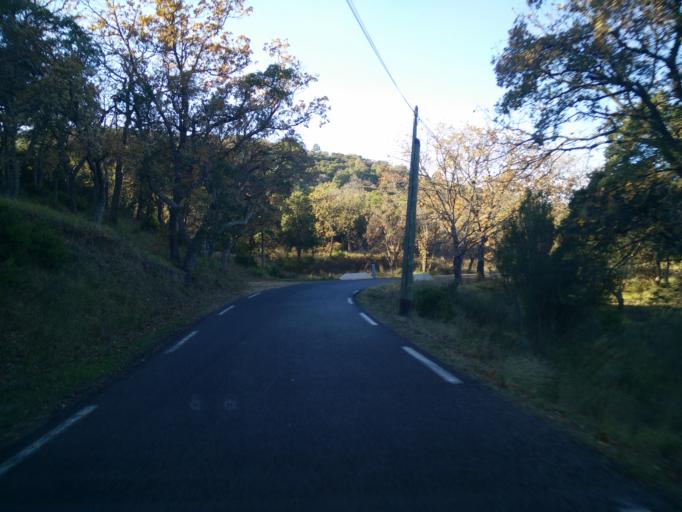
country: FR
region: Provence-Alpes-Cote d'Azur
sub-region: Departement du Var
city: Le Plan-de-la-Tour
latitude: 43.2917
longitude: 6.5666
